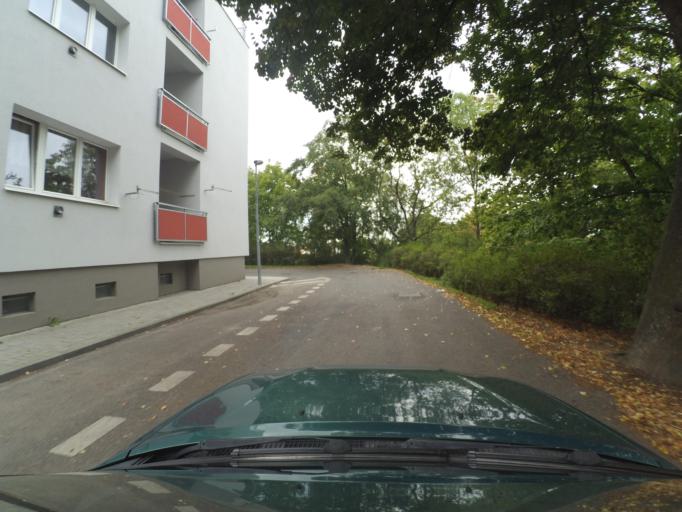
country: CZ
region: Ustecky
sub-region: Okres Louny
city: Louny
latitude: 50.3557
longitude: 13.8107
